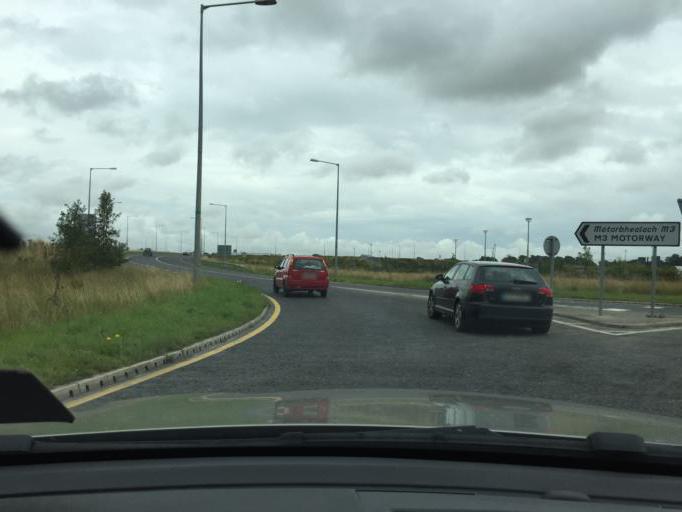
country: IE
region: Leinster
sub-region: An Mhi
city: Dunboyne
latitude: 53.4350
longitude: -6.4738
